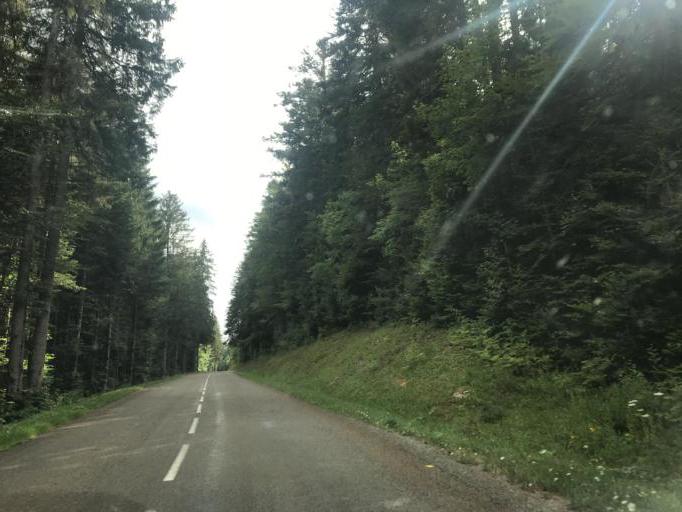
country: FR
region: Franche-Comte
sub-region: Departement du Jura
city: Valfin-les-Saint-Claude
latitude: 46.4890
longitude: 5.8447
